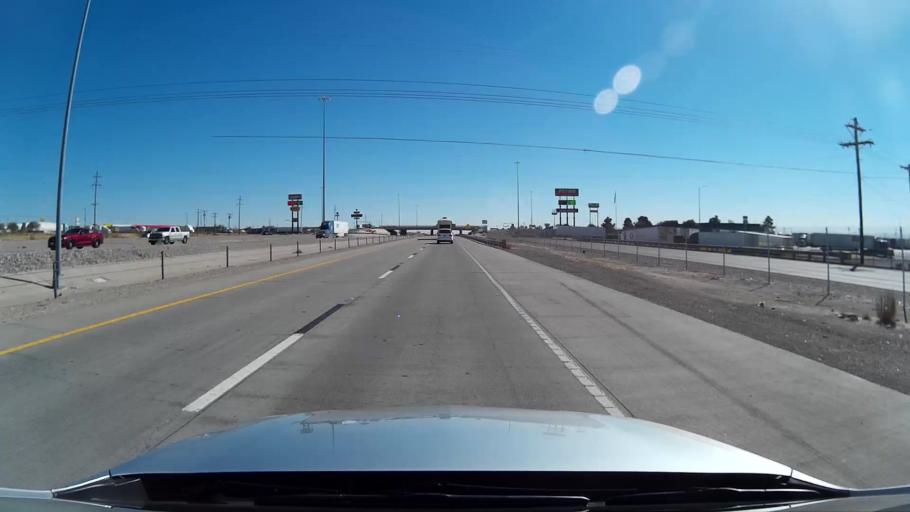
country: US
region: Texas
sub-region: El Paso County
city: Sparks
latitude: 31.6628
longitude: -106.2424
